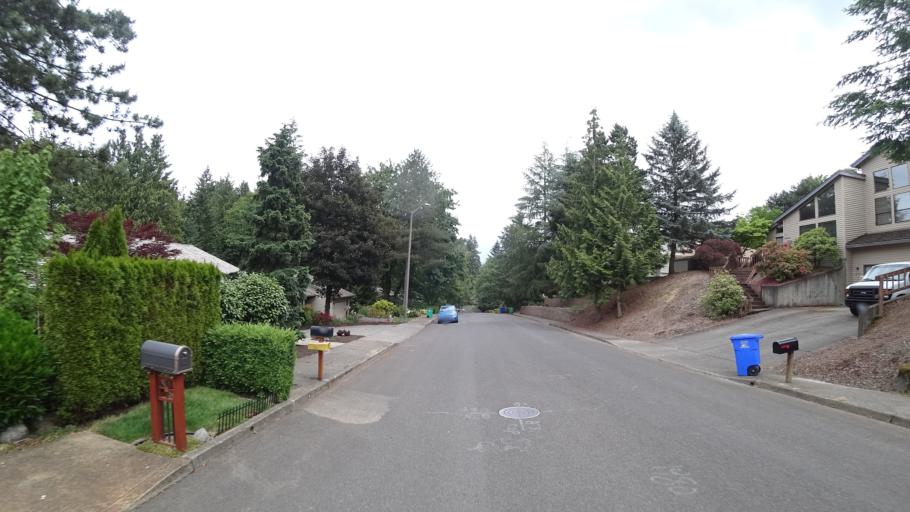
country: US
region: Oregon
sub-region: Clackamas County
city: Lake Oswego
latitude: 45.4540
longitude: -122.6977
